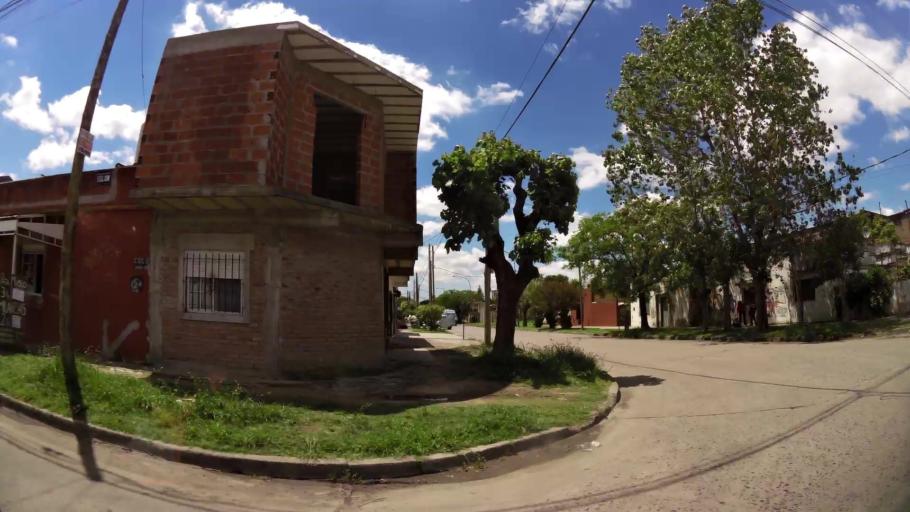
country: AR
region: Buenos Aires
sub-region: Partido de Lanus
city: Lanus
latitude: -34.7095
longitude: -58.4260
